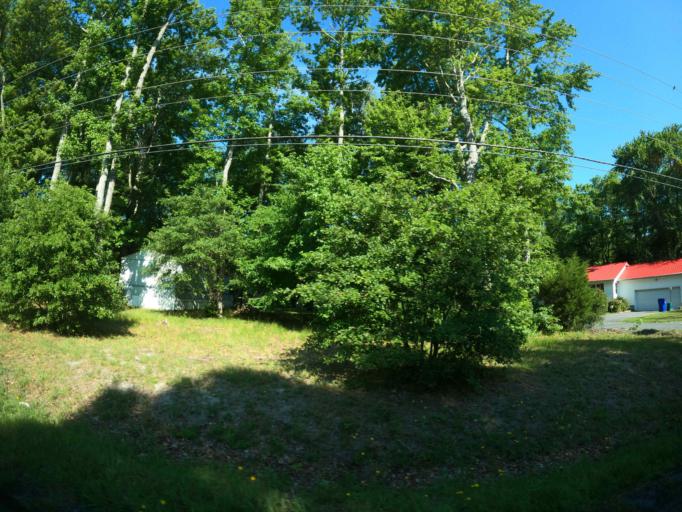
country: US
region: Delaware
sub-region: Sussex County
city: Ocean View
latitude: 38.5277
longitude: -75.0927
